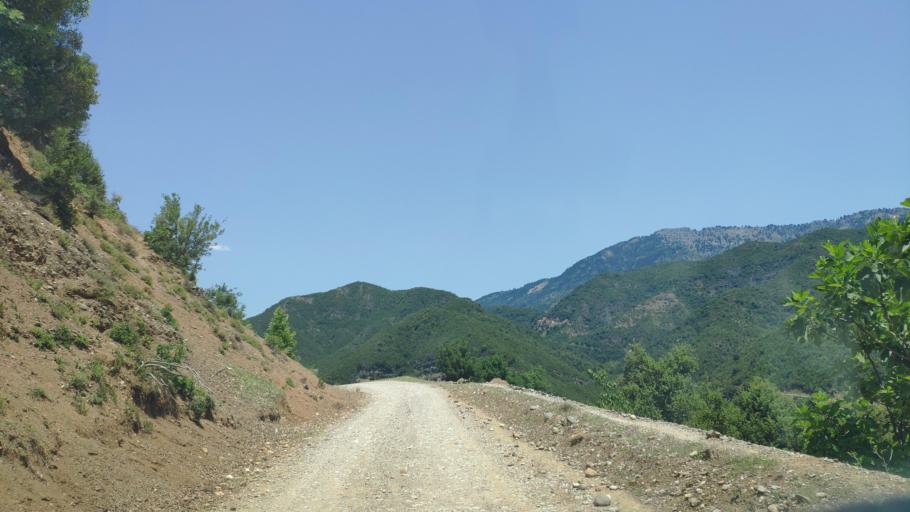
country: GR
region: Thessaly
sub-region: Nomos Kardhitsas
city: Anthiro
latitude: 39.1754
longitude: 21.3702
